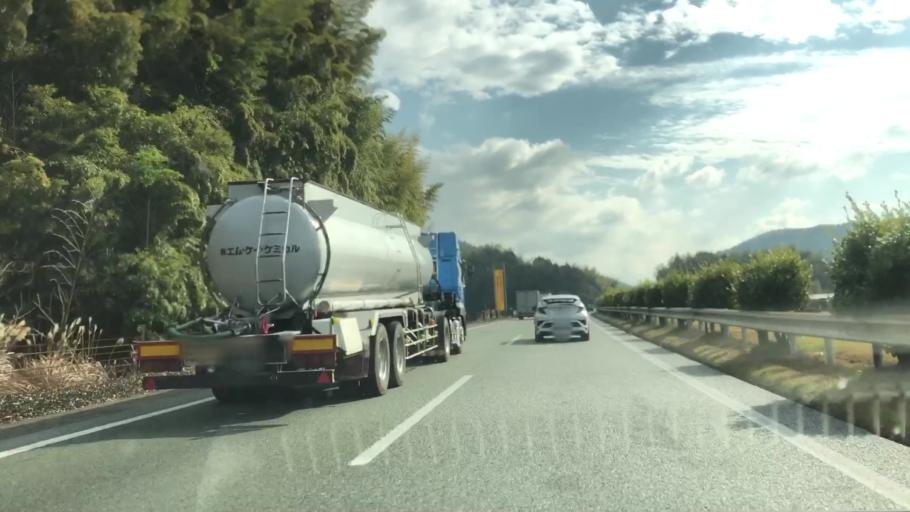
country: JP
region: Fukuoka
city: Setakamachi-takayanagi
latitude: 33.1083
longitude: 130.5332
